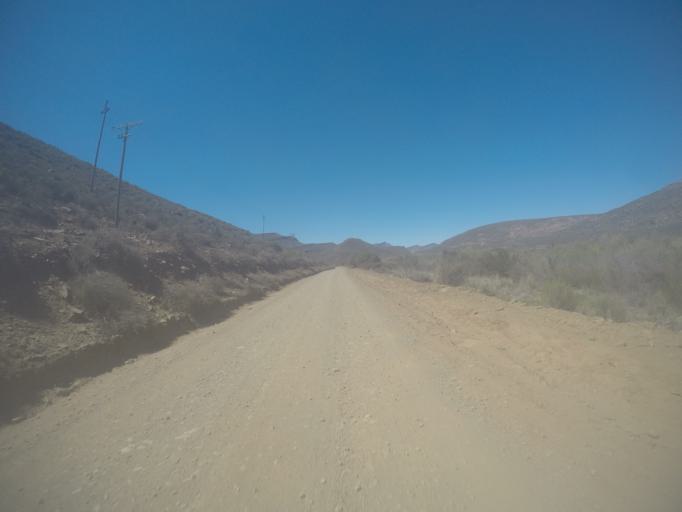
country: ZA
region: Western Cape
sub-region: West Coast District Municipality
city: Clanwilliam
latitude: -32.5162
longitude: 19.3484
